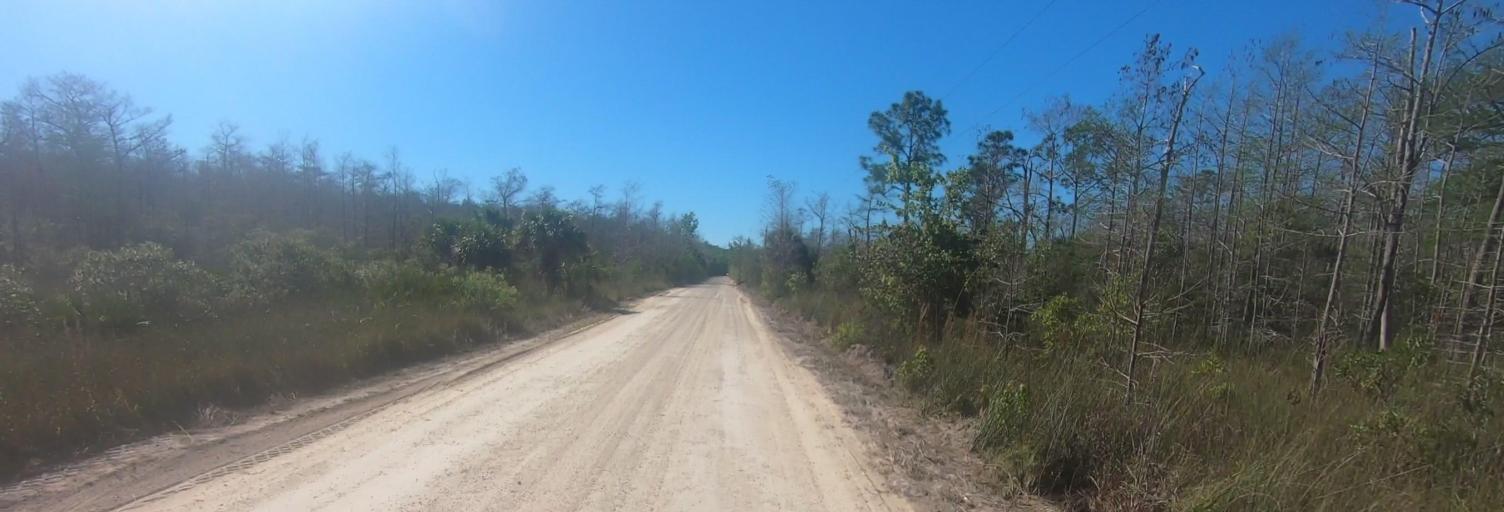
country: US
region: Florida
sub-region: Collier County
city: Marco
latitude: 25.8825
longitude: -81.2298
